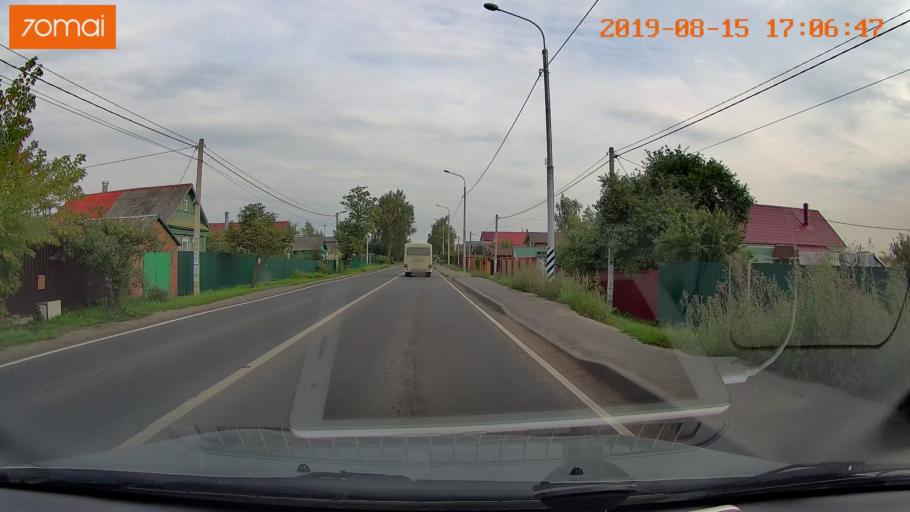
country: RU
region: Moskovskaya
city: Beloozerskiy
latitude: 55.4682
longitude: 38.4166
